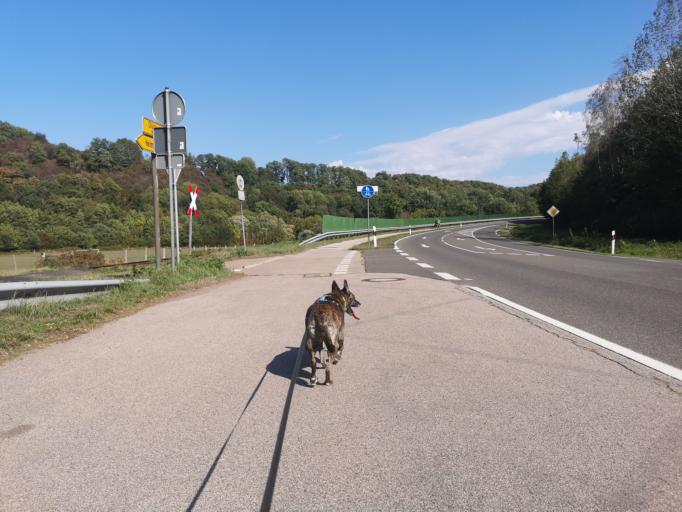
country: DE
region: North Rhine-Westphalia
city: Heimbach
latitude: 50.6502
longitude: 6.4771
